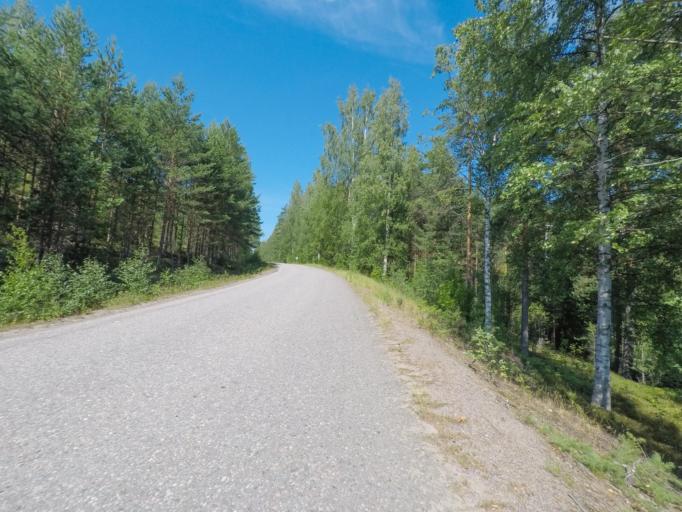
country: FI
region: Southern Savonia
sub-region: Mikkeli
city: Puumala
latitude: 61.4104
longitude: 28.0926
